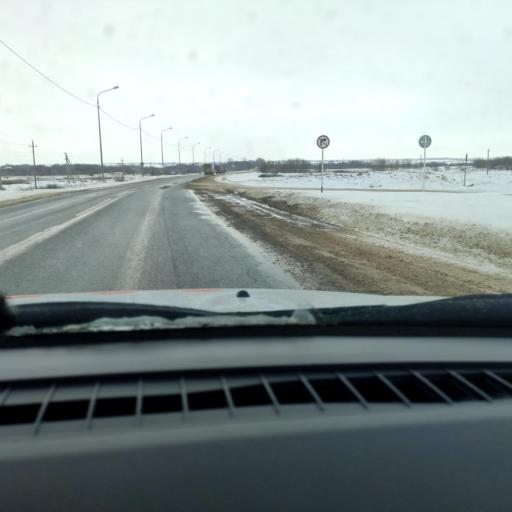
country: RU
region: Samara
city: Dubovyy Umet
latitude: 52.8216
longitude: 50.5022
